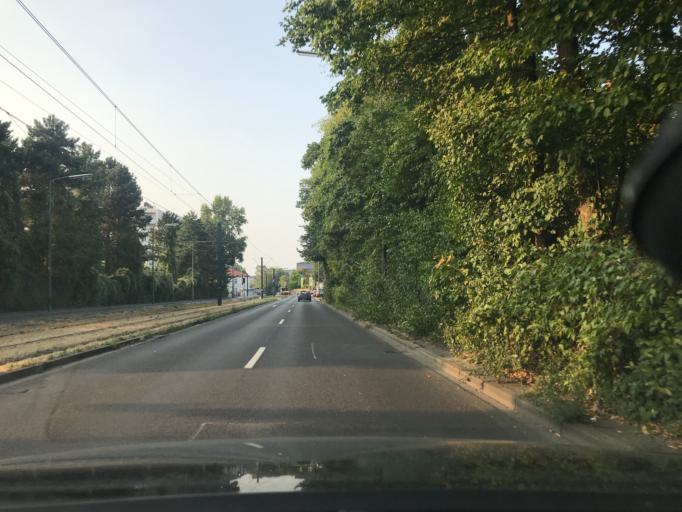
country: DE
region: North Rhine-Westphalia
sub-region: Regierungsbezirk Dusseldorf
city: Ratingen
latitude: 51.2525
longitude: 6.8224
